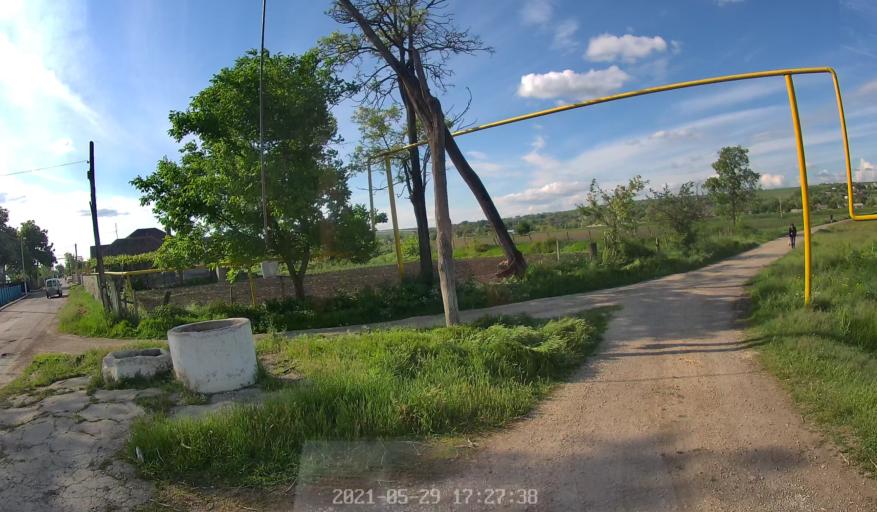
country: MD
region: Laloveni
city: Ialoveni
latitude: 46.8322
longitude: 28.8394
